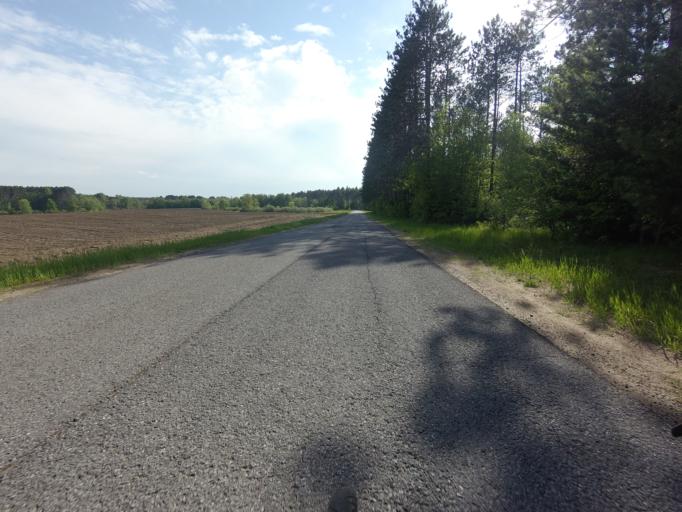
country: US
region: New York
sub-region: St. Lawrence County
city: Gouverneur
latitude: 44.1955
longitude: -75.2676
